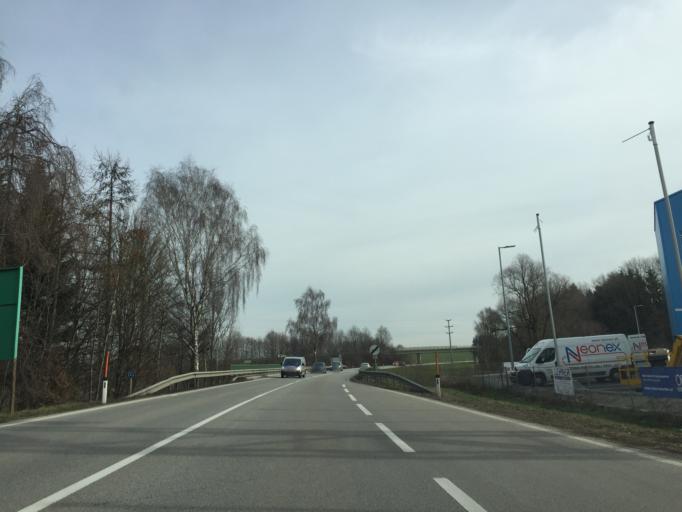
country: AT
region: Upper Austria
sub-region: Politischer Bezirk Ried im Innkreis
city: Ried im Innkreis
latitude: 48.2238
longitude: 13.4802
